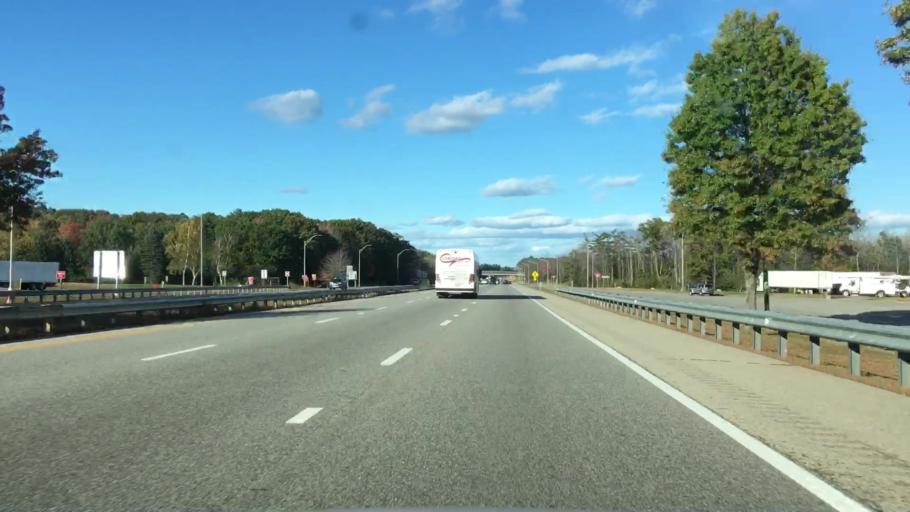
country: US
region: Maine
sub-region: York County
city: West Kennebunk
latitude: 43.4107
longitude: -70.5592
